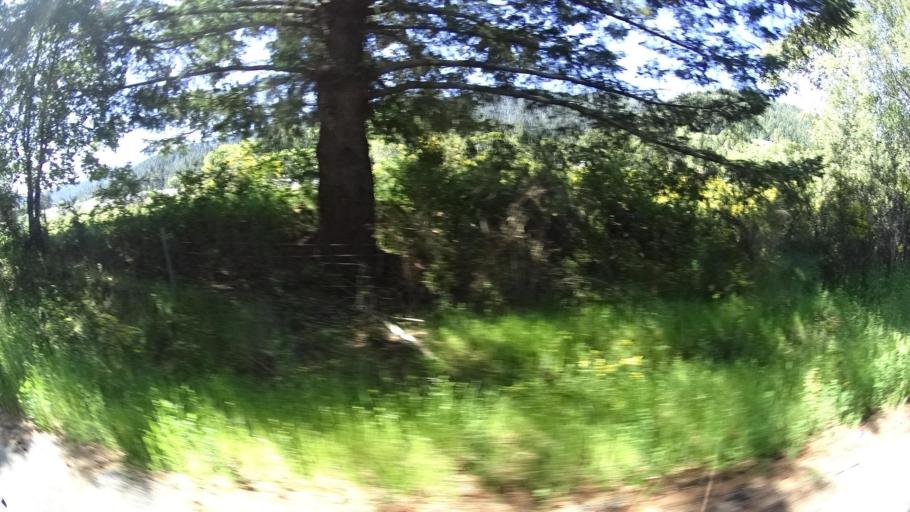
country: US
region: California
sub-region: Humboldt County
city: Rio Dell
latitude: 40.2472
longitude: -124.1669
